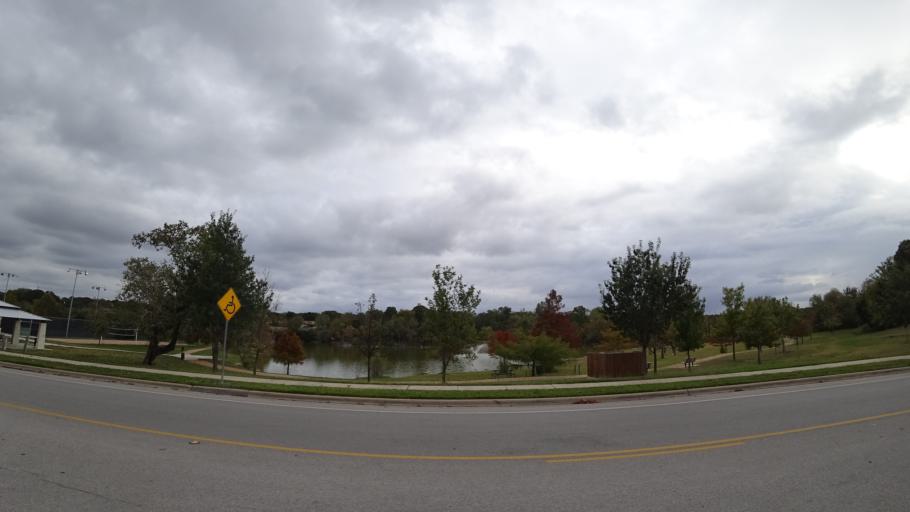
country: US
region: Texas
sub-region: Williamson County
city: Round Rock
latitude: 30.5034
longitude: -97.6932
